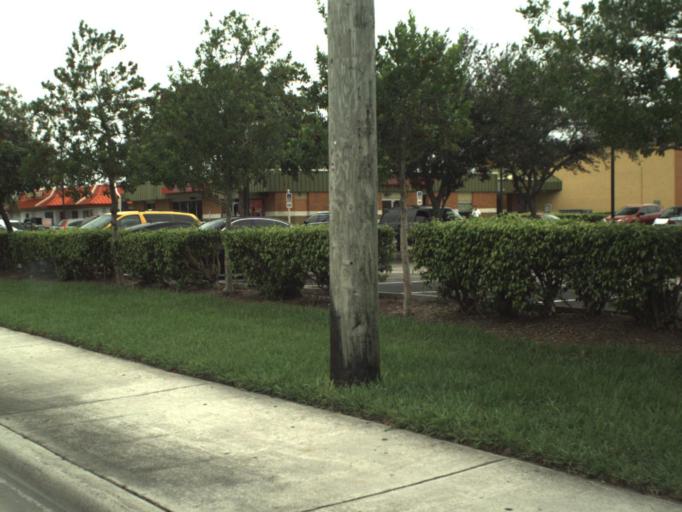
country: US
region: Florida
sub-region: Palm Beach County
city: Schall Circle
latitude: 26.7047
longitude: -80.1113
